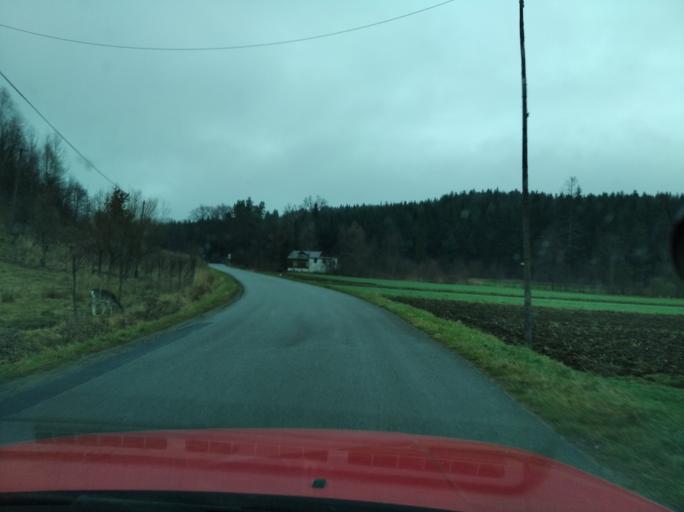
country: PL
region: Subcarpathian Voivodeship
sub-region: Powiat przemyski
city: Nienadowa
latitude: 49.8572
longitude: 22.4261
